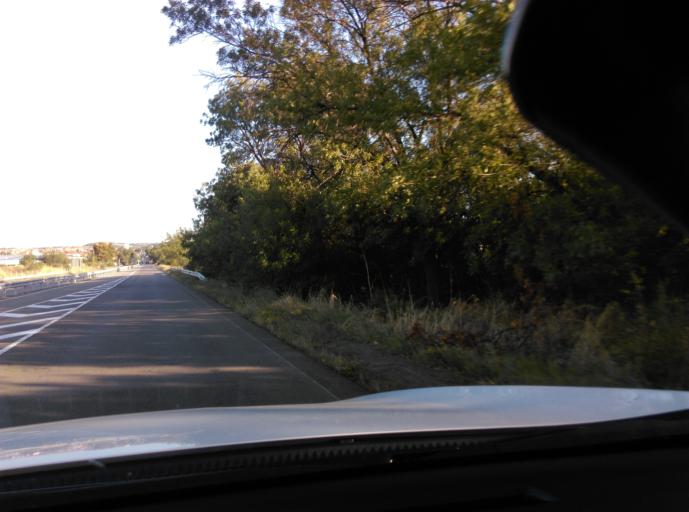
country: BG
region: Burgas
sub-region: Obshtina Kameno
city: Kameno
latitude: 42.5961
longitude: 27.3921
